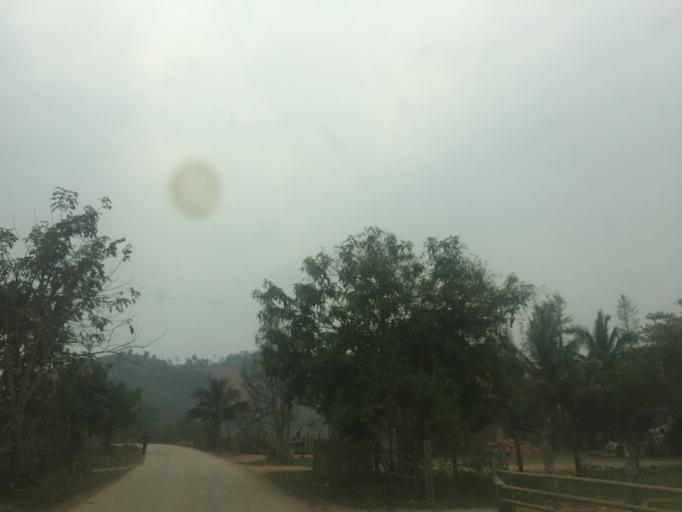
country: LA
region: Vientiane
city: Muang Sanakham
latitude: 18.3871
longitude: 101.5293
